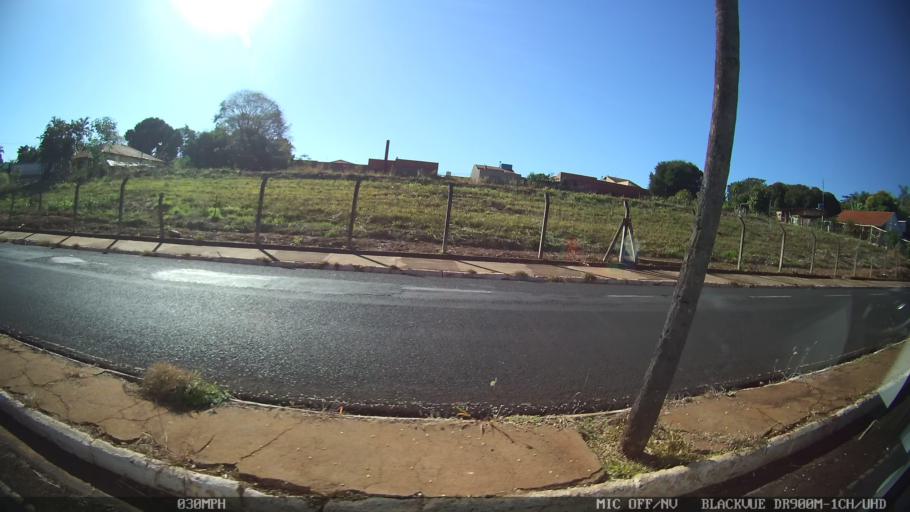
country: BR
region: Sao Paulo
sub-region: Olimpia
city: Olimpia
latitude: -20.7432
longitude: -48.9000
